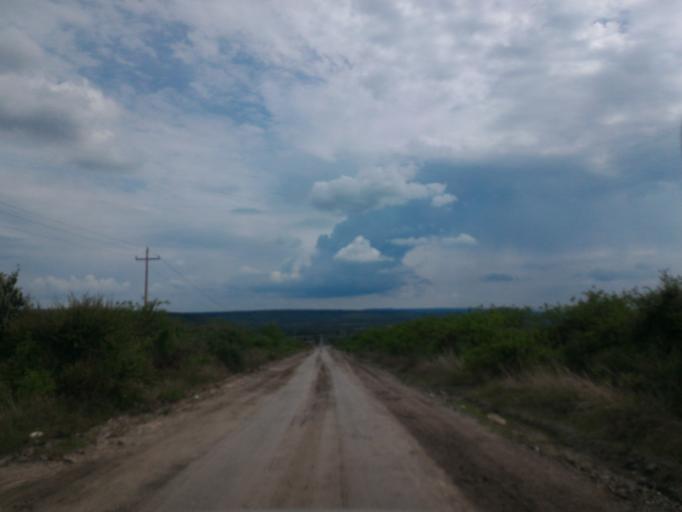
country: MX
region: Jalisco
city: San Diego de Alejandria
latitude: 20.9087
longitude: -102.0464
